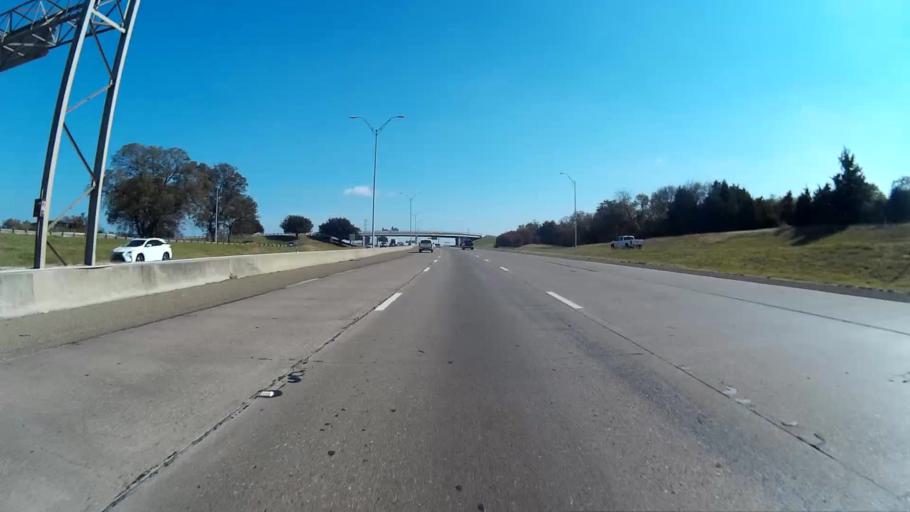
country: US
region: Texas
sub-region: Dallas County
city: Hutchins
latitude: 32.6593
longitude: -96.7236
